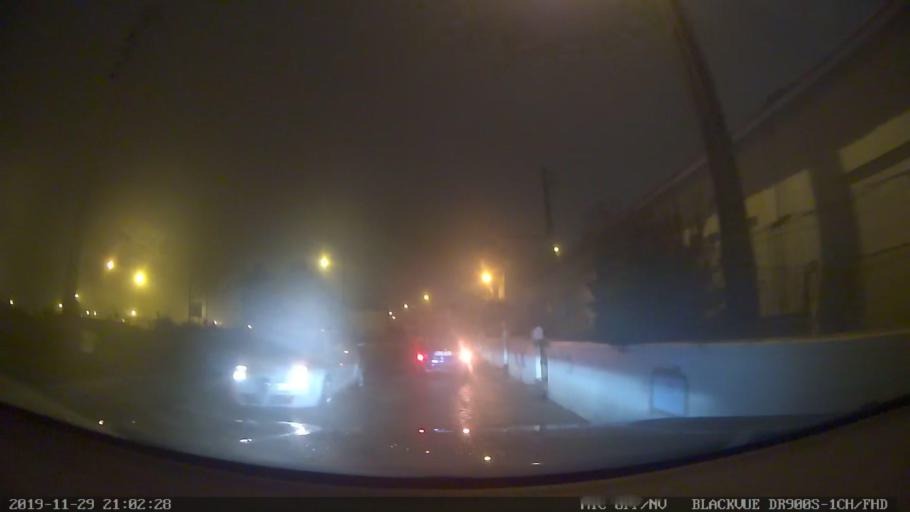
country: PT
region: Porto
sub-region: Matosinhos
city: Santa Cruz do Bispo
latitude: 41.2094
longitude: -8.6810
